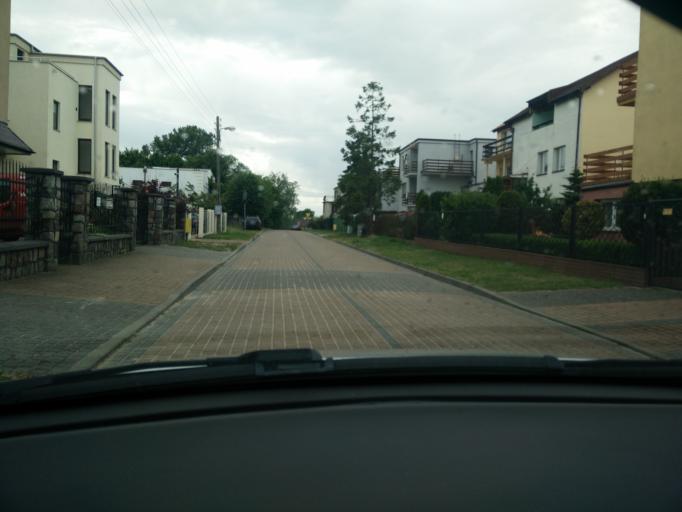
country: PL
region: Pomeranian Voivodeship
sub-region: Powiat pucki
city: Mosty
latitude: 54.6306
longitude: 18.5022
